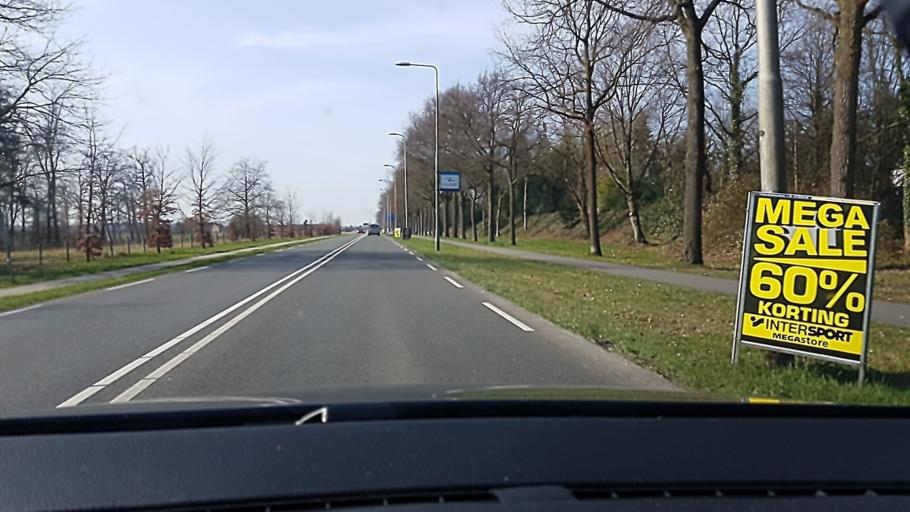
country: NL
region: Limburg
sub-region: Gemeente Roermond
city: Roermond
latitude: 51.1814
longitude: 5.9849
